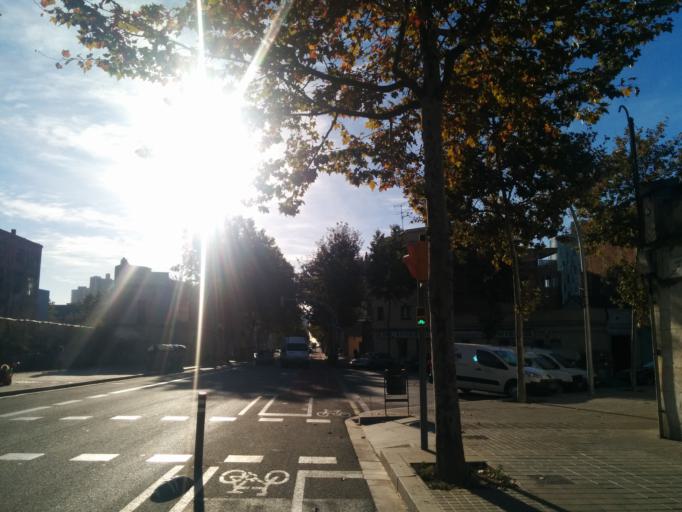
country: ES
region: Catalonia
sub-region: Provincia de Barcelona
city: Sant Marti
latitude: 41.4146
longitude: 2.2080
